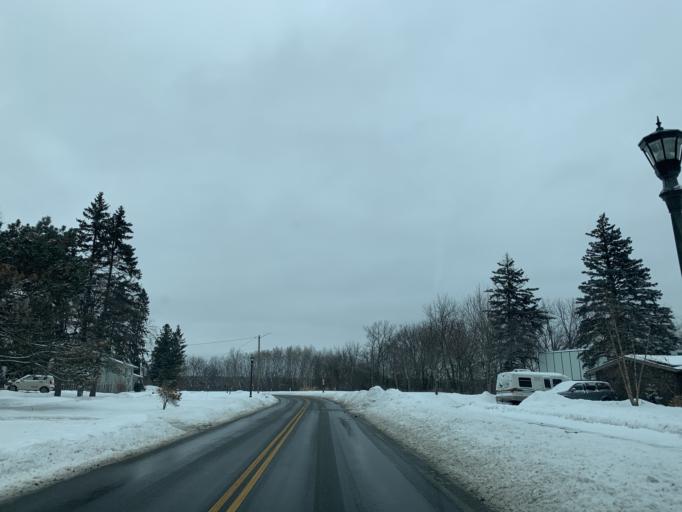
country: US
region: Minnesota
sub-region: Ramsey County
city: Roseville
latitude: 44.9875
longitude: -93.1142
